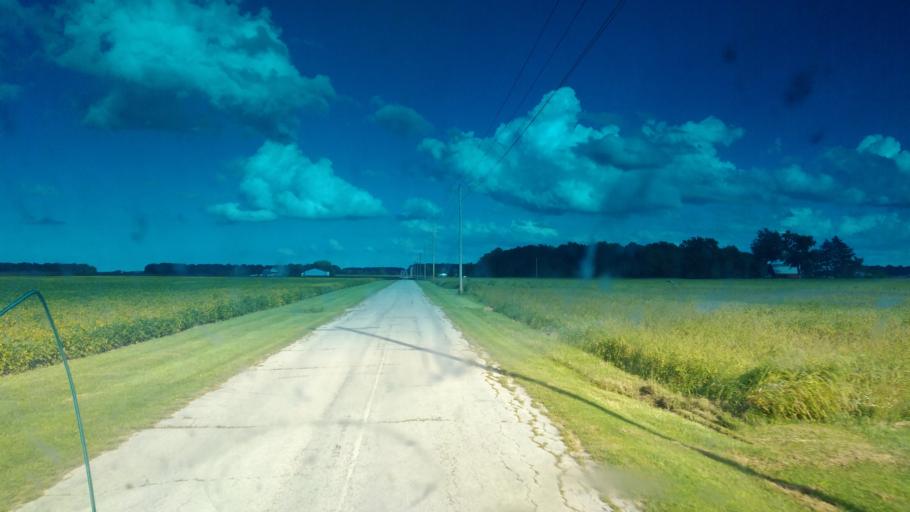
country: US
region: Ohio
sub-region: Hancock County
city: Arlington
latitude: 40.9364
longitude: -83.7574
